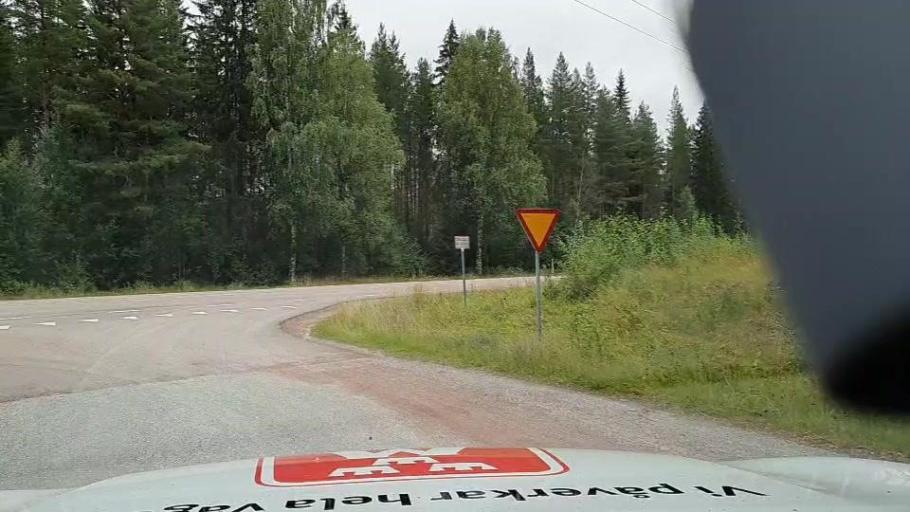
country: SE
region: Jaemtland
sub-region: Ragunda Kommun
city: Hammarstrand
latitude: 63.1728
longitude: 15.8740
